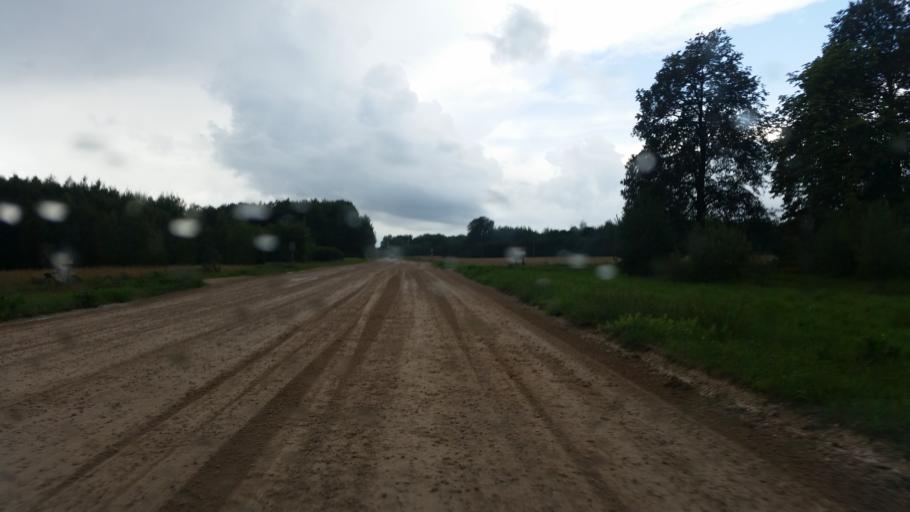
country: LV
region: Vecumnieki
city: Vecumnieki
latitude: 56.4314
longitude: 24.4497
